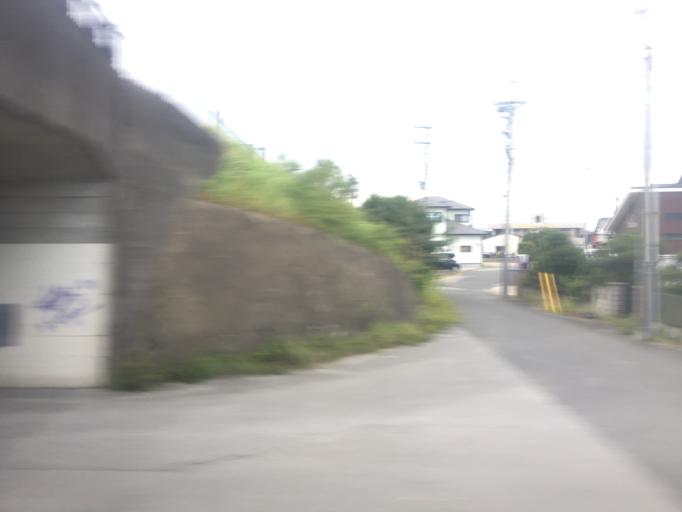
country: JP
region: Chiba
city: Kisarazu
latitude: 35.3687
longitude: 139.9244
